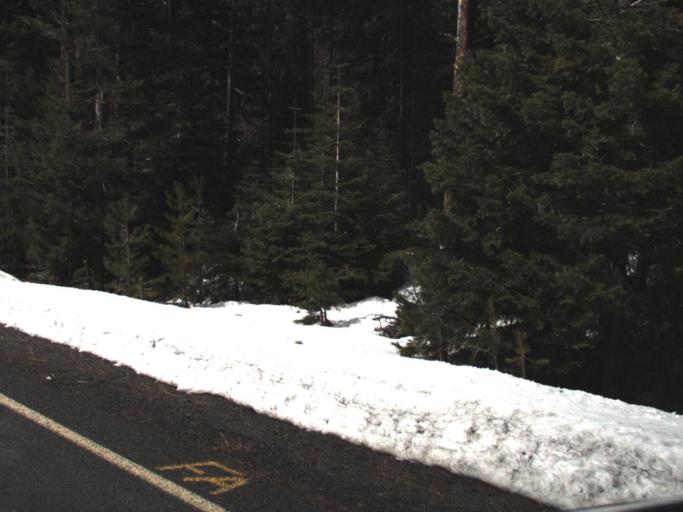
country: US
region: Washington
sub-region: Kittitas County
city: Cle Elum
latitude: 46.9359
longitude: -121.3507
